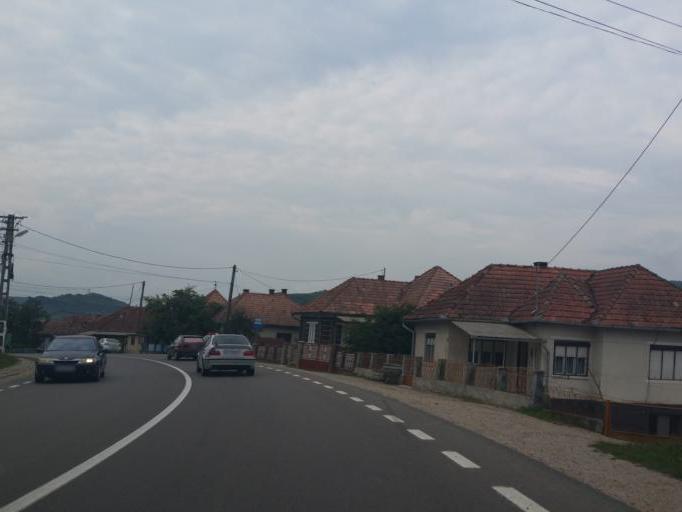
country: RO
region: Salaj
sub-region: Comuna Hida
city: Hida
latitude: 47.0349
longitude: 23.2704
